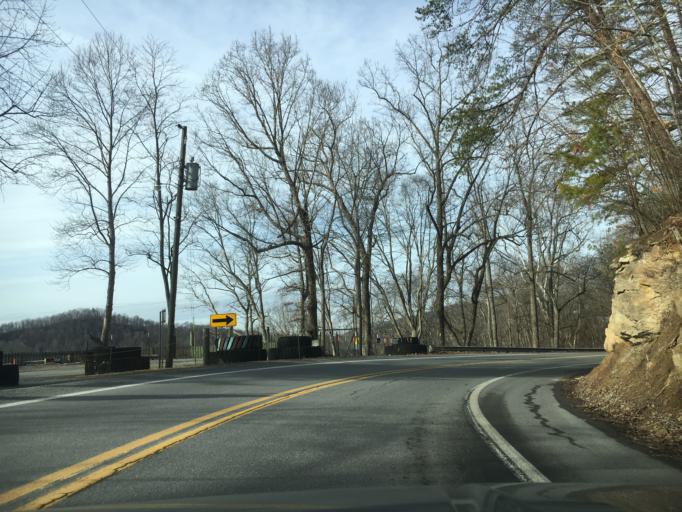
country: US
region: West Virginia
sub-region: Fayette County
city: Ansted
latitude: 38.1241
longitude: -81.1409
